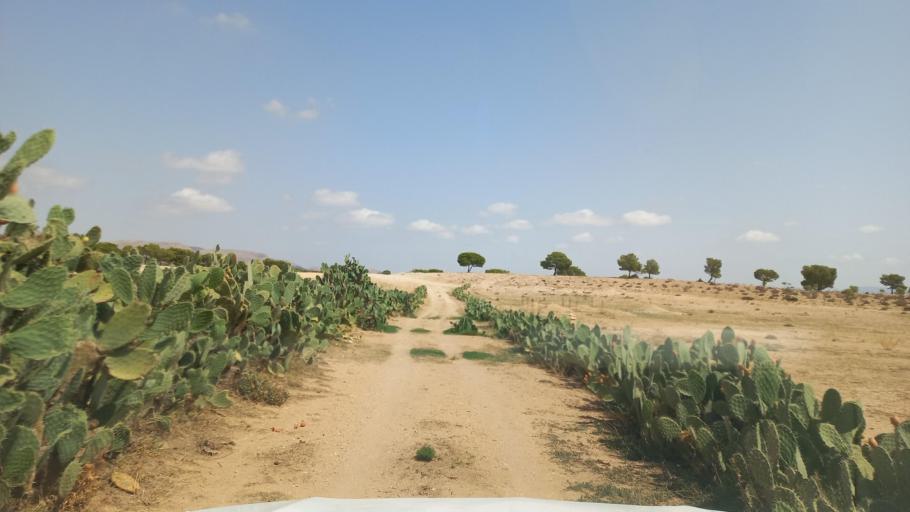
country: TN
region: Al Qasrayn
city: Sbiba
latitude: 35.3950
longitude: 8.9852
